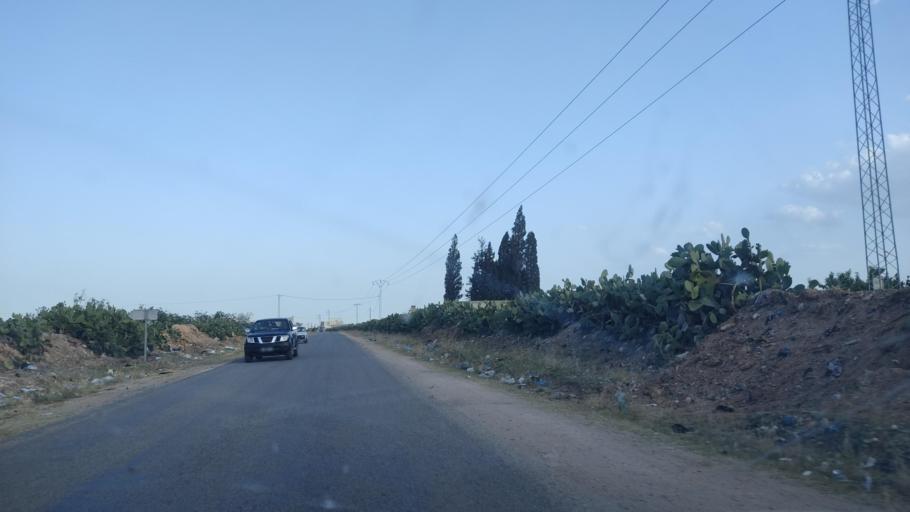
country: TN
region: Safaqis
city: Sfax
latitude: 34.8149
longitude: 10.6570
